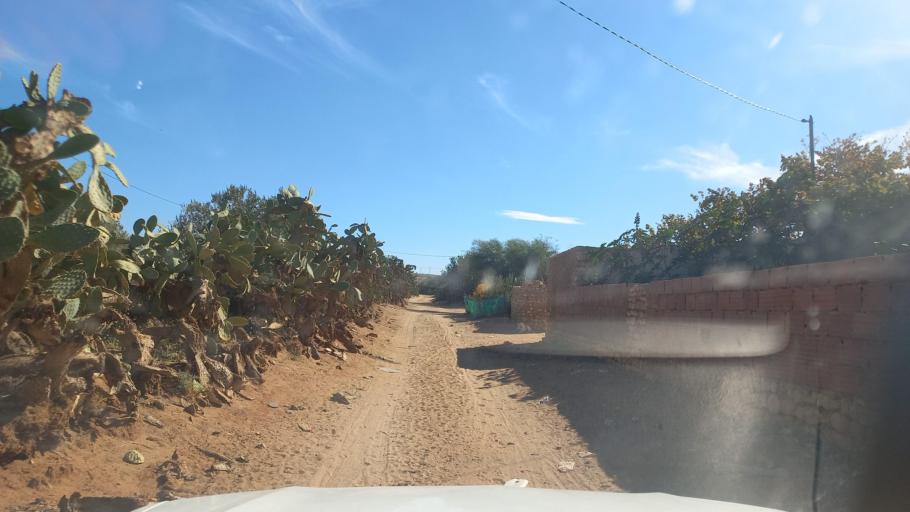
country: TN
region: Al Qasrayn
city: Kasserine
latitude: 35.2106
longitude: 8.9713
